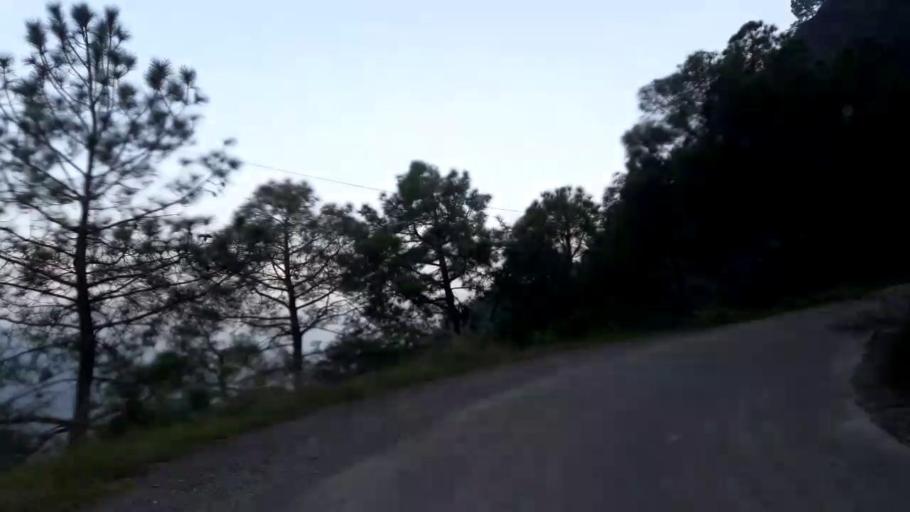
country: IN
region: Himachal Pradesh
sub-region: Shimla
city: Shimla
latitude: 31.0590
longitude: 77.1558
